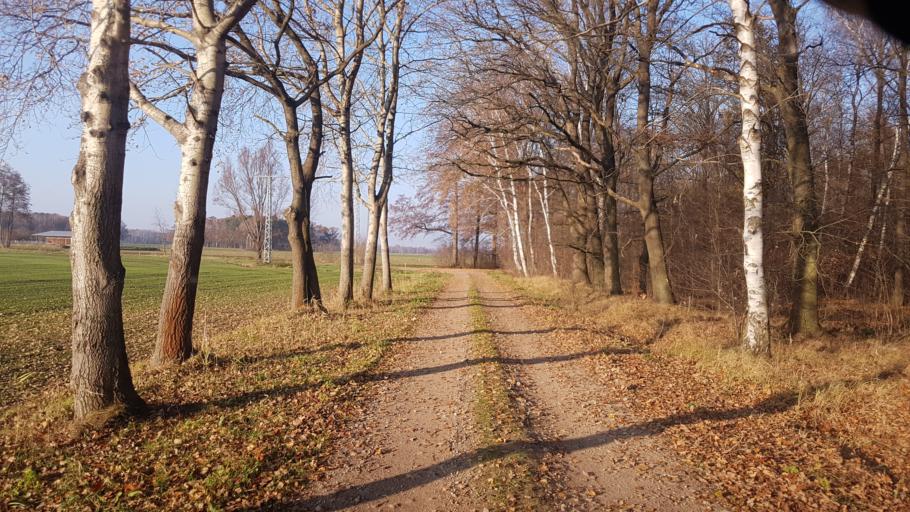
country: DE
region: Brandenburg
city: Tettau
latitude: 51.4406
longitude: 13.7284
